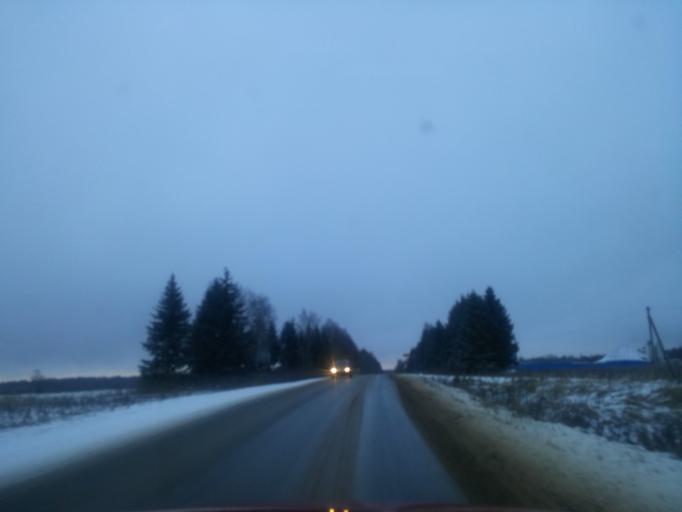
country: RU
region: Tverskaya
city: Likhoslavl'
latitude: 56.9939
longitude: 35.4439
